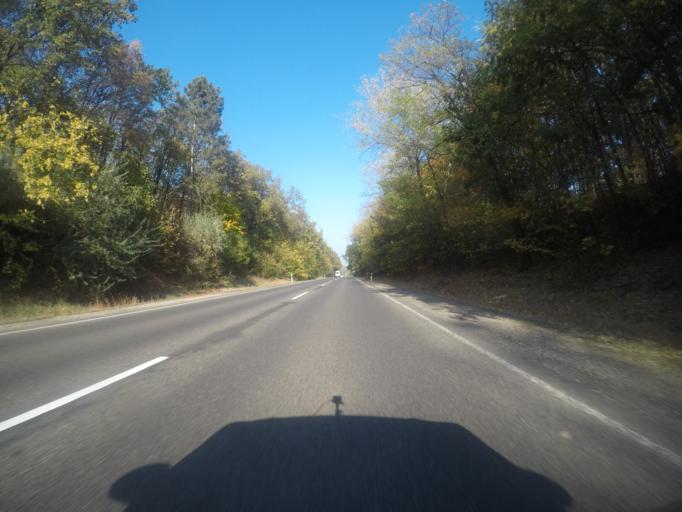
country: HU
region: Fejer
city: dunaujvaros
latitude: 46.9864
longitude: 18.9176
